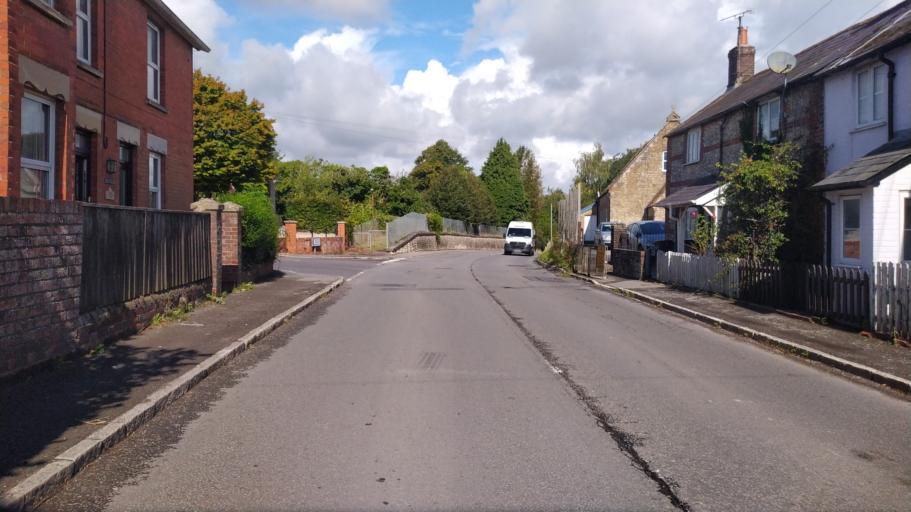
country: GB
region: England
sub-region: Dorset
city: Manston
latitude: 50.9014
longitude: -2.2517
